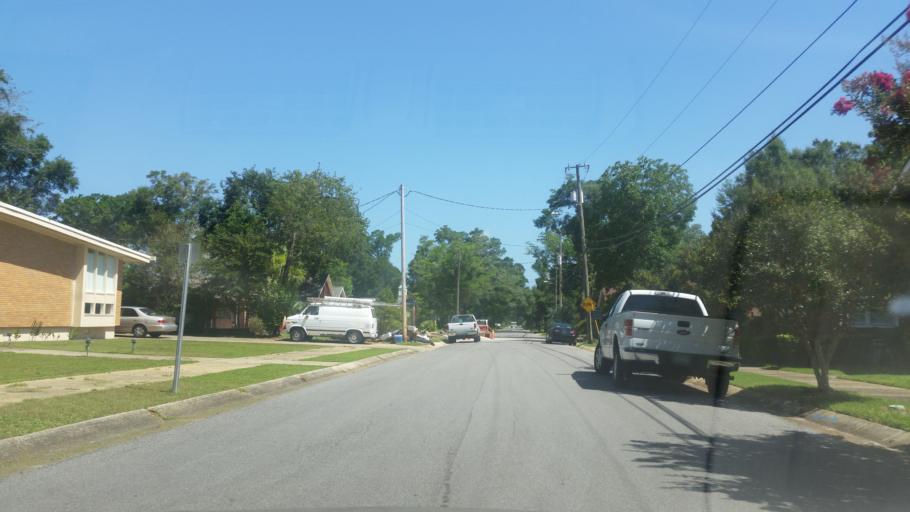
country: US
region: Florida
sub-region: Escambia County
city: Pensacola
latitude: 30.4294
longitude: -87.2220
